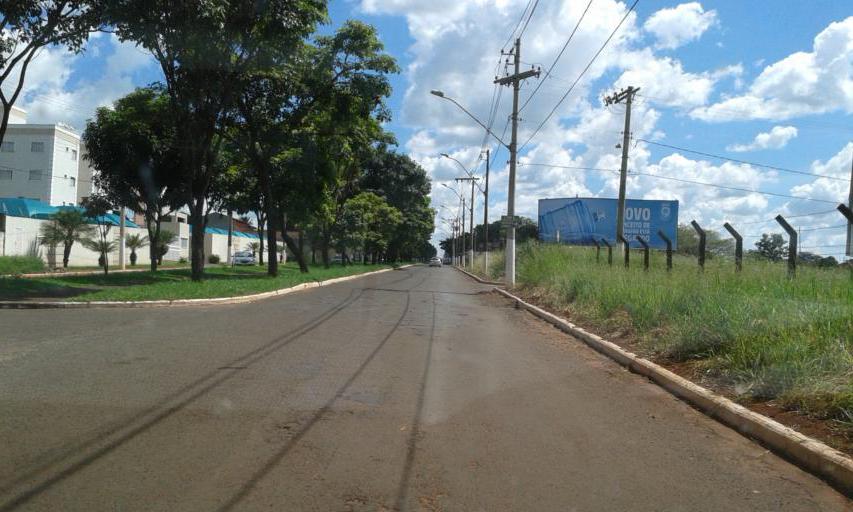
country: BR
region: Minas Gerais
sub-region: Ituiutaba
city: Ituiutaba
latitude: -18.9694
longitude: -49.4761
